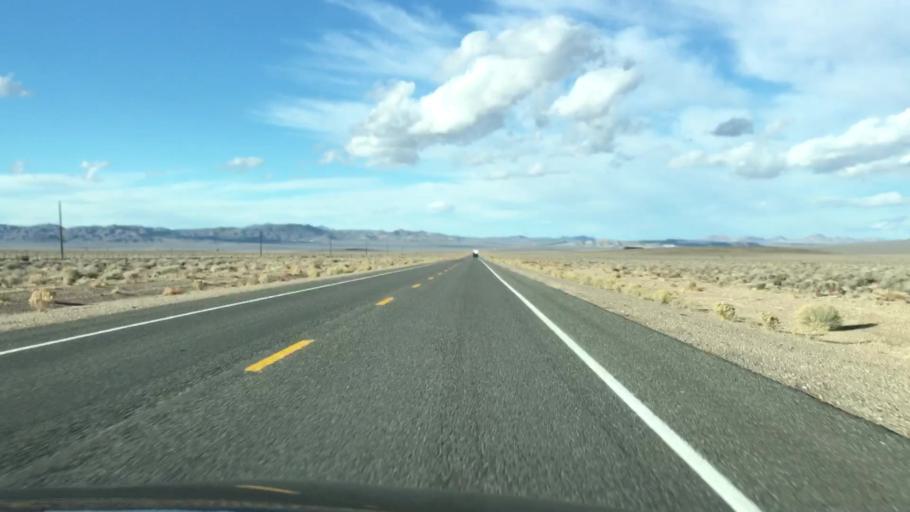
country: US
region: Nevada
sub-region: Esmeralda County
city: Goldfield
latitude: 37.4042
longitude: -117.1502
